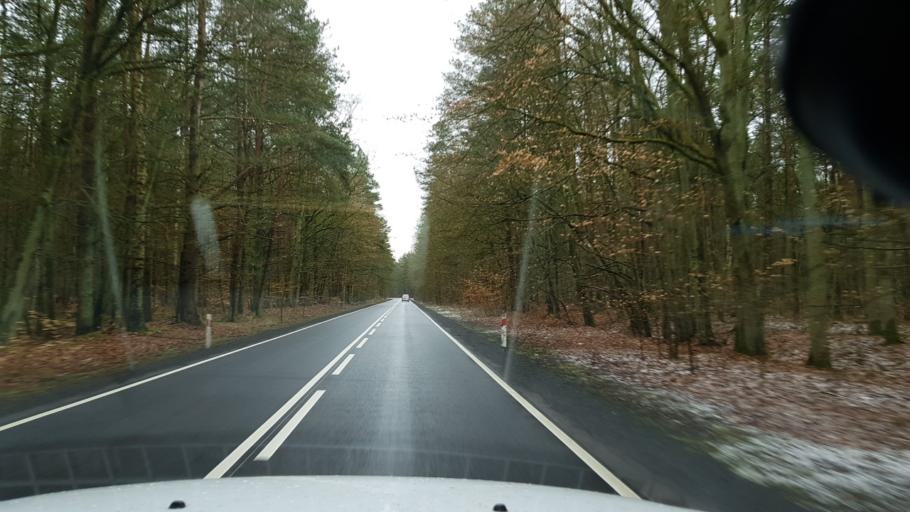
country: PL
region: West Pomeranian Voivodeship
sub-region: Powiat goleniowski
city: Stepnica
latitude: 53.6397
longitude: 14.6612
